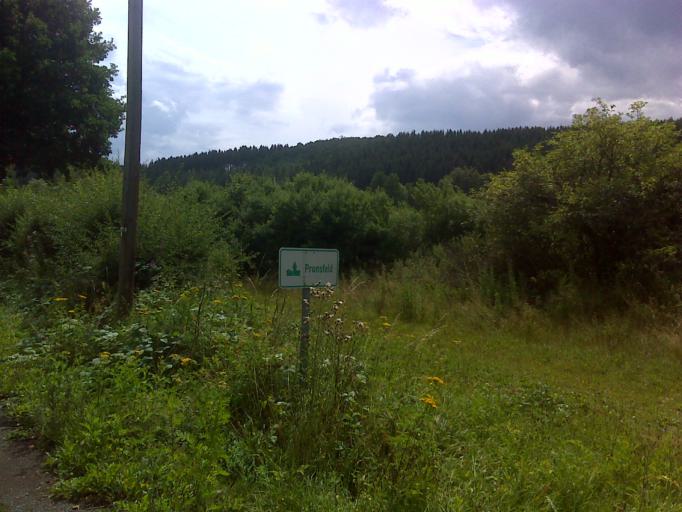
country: DE
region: Rheinland-Pfalz
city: Pronsfeld
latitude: 50.1622
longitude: 6.3213
